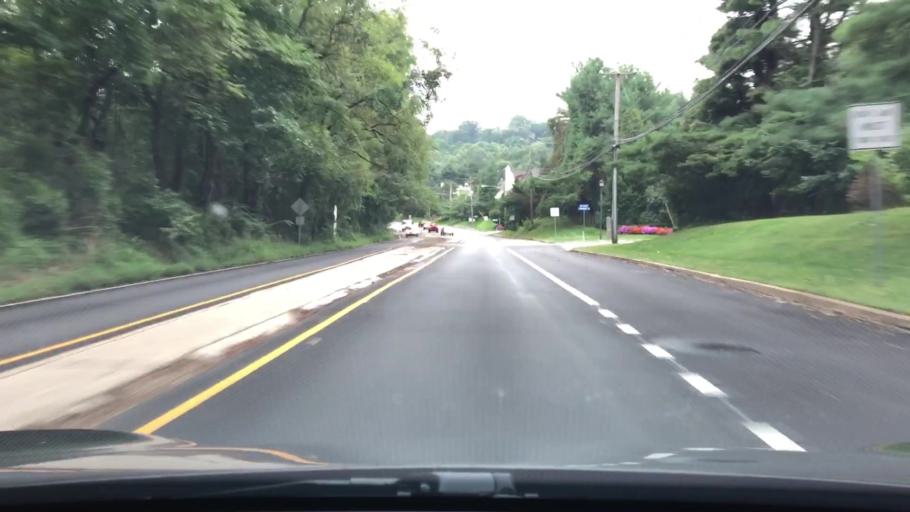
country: US
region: Pennsylvania
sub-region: Delaware County
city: Broomall
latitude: 40.0004
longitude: -75.3600
